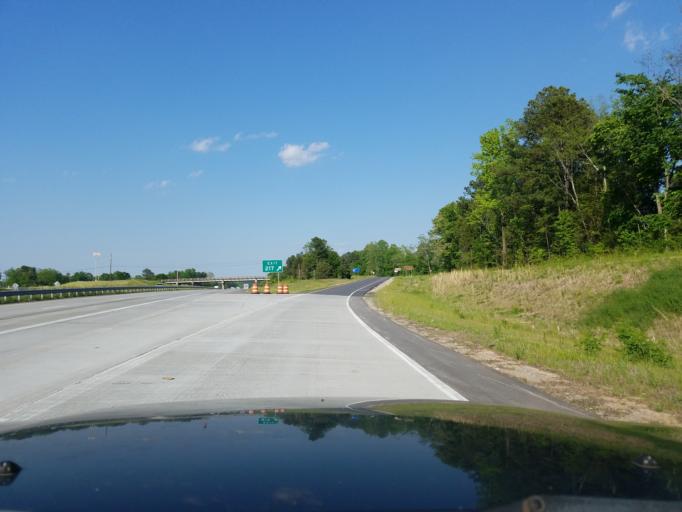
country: US
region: North Carolina
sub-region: Vance County
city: Henderson
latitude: 36.3600
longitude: -78.3768
